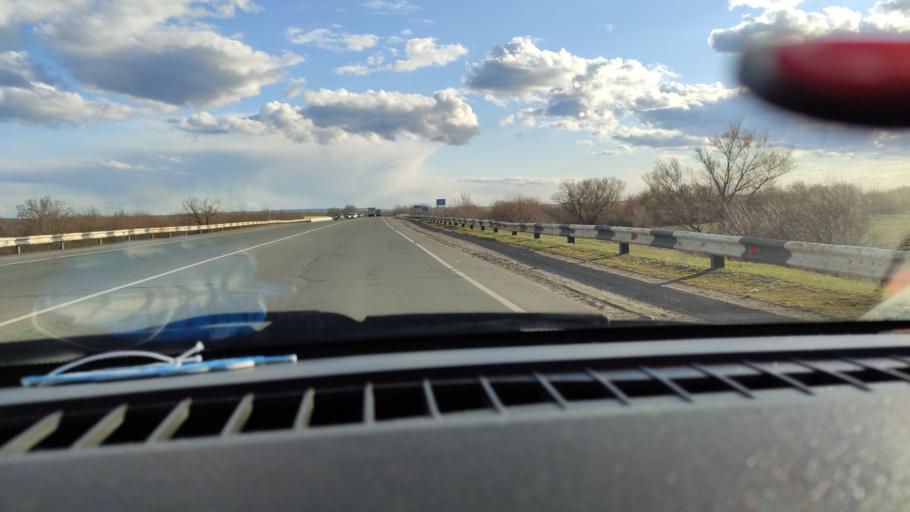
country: RU
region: Saratov
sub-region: Saratovskiy Rayon
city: Saratov
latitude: 51.7240
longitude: 46.0279
